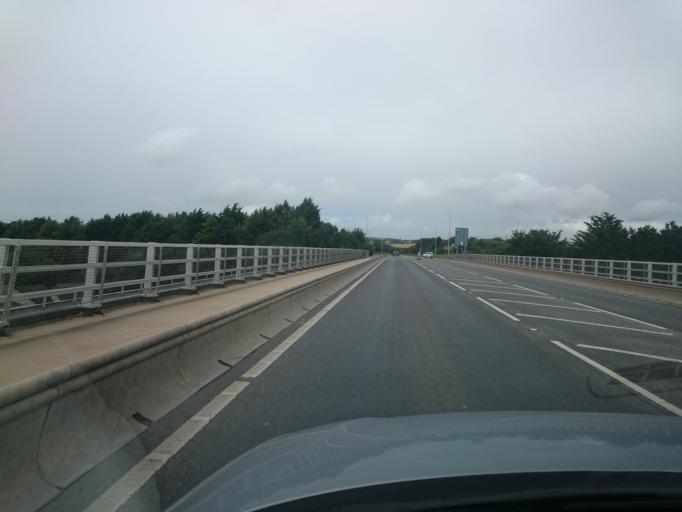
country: GB
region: Wales
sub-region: Pembrokeshire
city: Burton
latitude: 51.7096
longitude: -4.9352
